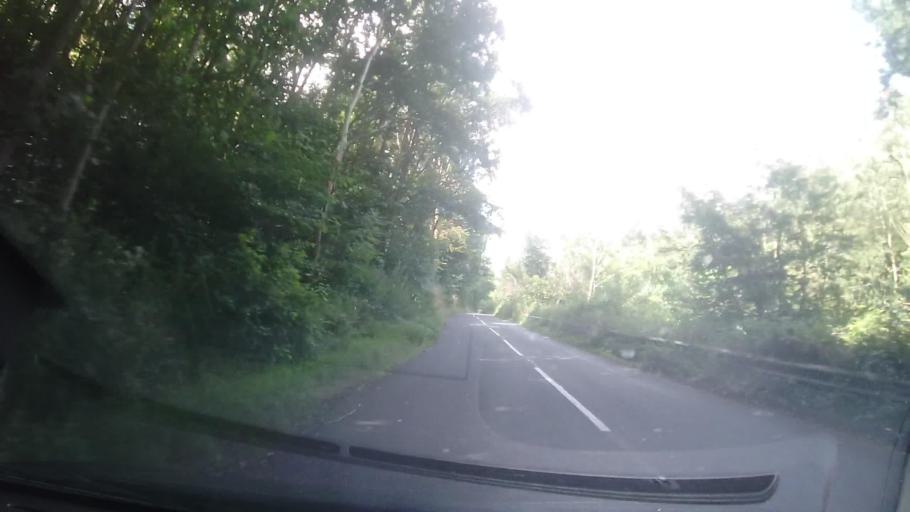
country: GB
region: Wales
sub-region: Sir Powys
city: Knighton
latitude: 52.3624
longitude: -3.0478
